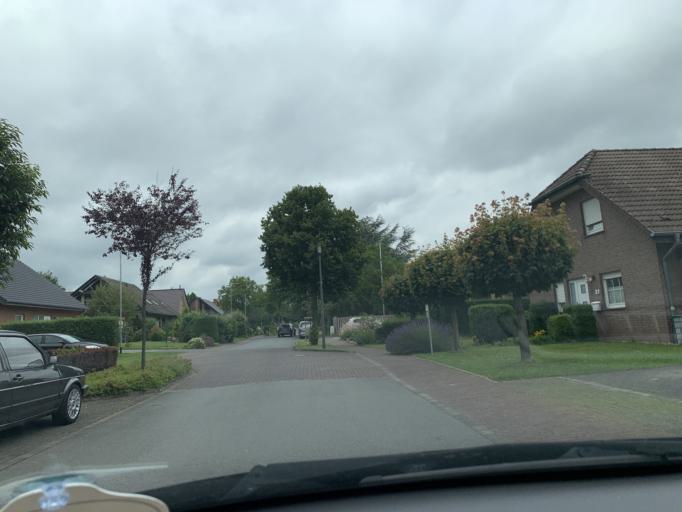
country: DE
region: North Rhine-Westphalia
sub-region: Regierungsbezirk Munster
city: Wadersloh
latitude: 51.7373
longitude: 8.2392
